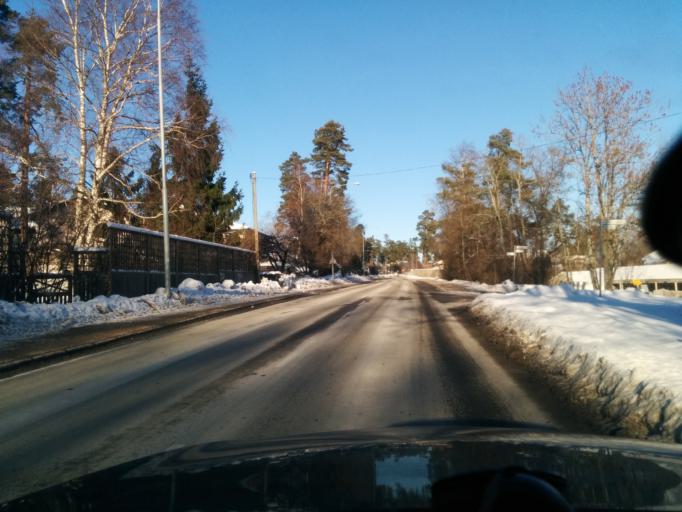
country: SE
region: Stockholm
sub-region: Taby Kommun
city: Taby
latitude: 59.4632
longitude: 18.0872
